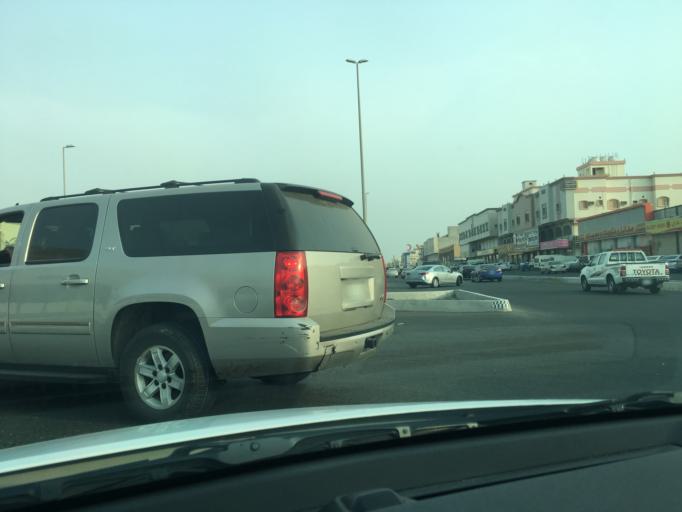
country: SA
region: Makkah
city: Jeddah
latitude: 21.7531
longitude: 39.1867
